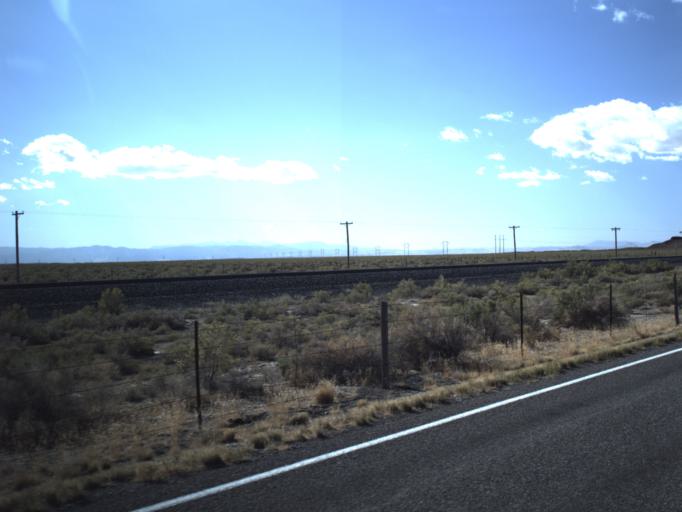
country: US
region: Utah
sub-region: Millard County
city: Delta
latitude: 39.1602
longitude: -112.7129
